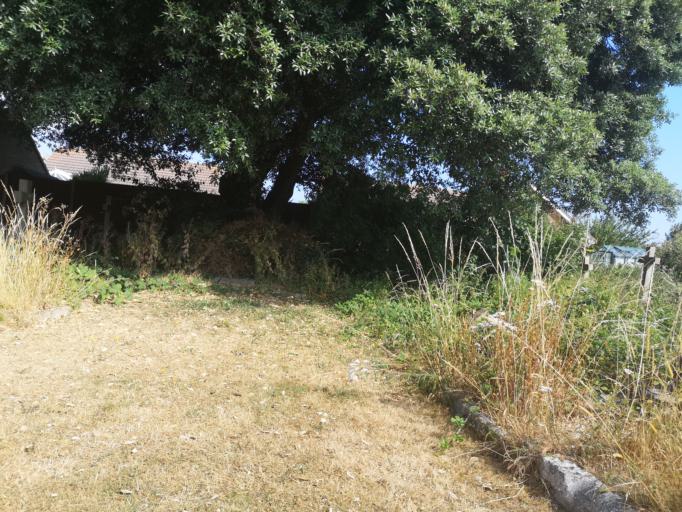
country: GB
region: England
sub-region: Isle of Wight
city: Bembridge
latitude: 50.6871
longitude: -1.0818
